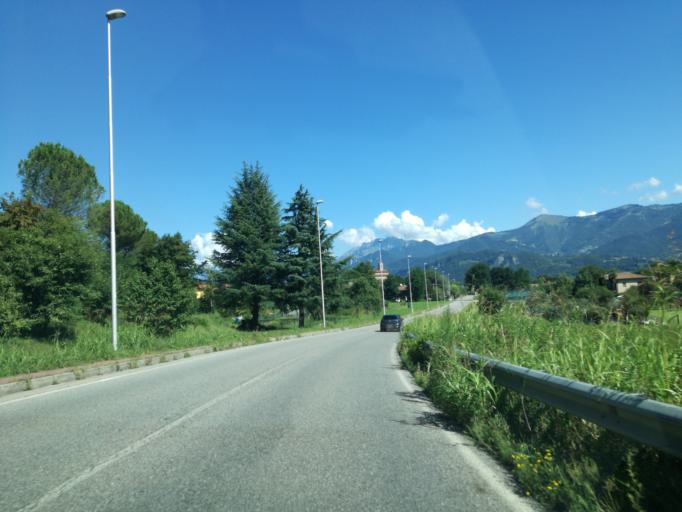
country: IT
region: Lombardy
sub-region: Provincia di Lecco
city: Arlate
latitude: 45.7159
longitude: 9.4436
